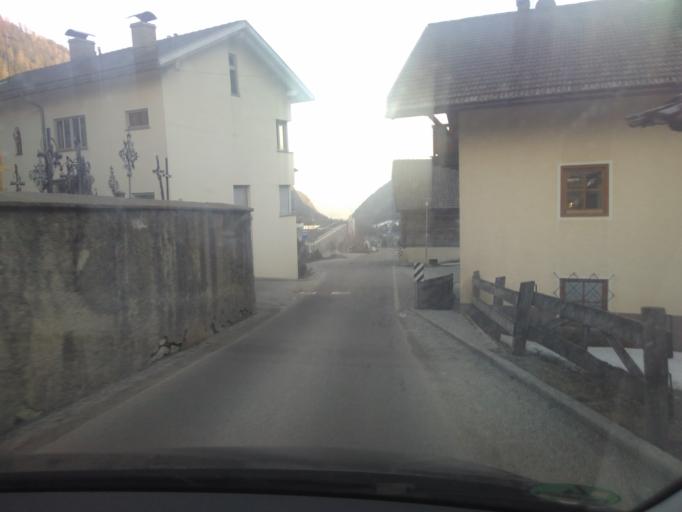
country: IT
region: Trentino-Alto Adige
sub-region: Bolzano
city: Fortezza
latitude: 46.8395
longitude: 11.6268
